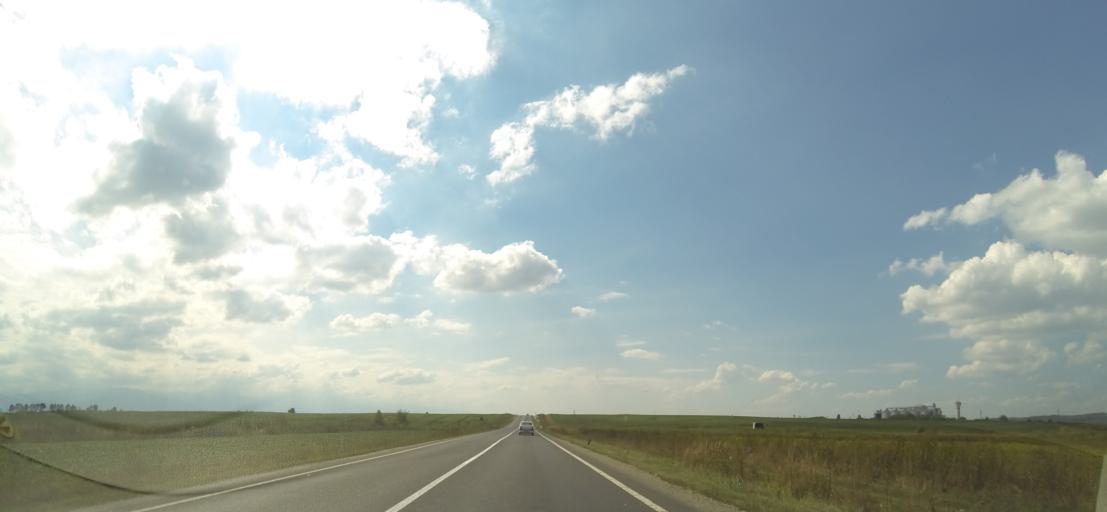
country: RO
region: Brasov
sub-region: Comuna Sercaia
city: Sercaia
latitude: 45.8307
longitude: 25.1242
